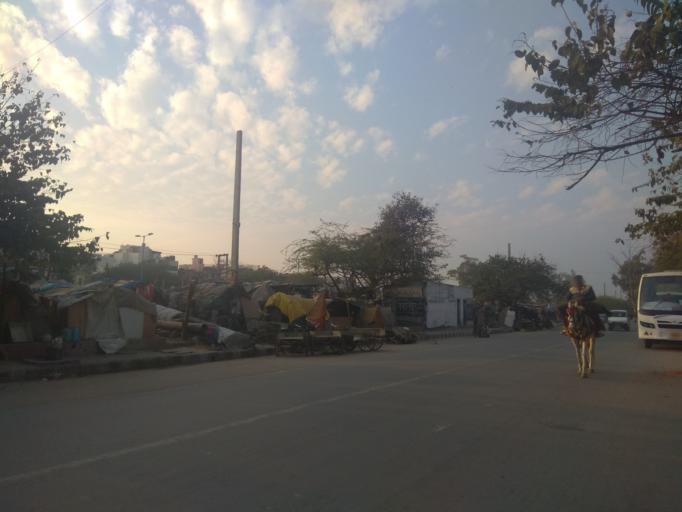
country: IN
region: NCT
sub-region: West Delhi
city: Nangloi Jat
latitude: 28.6352
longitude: 77.0624
